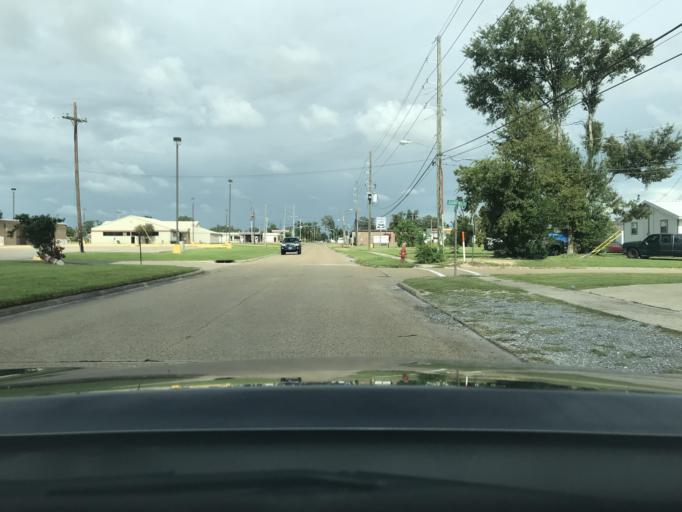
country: US
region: Louisiana
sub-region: Calcasieu Parish
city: Westlake
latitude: 30.2477
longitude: -93.2605
